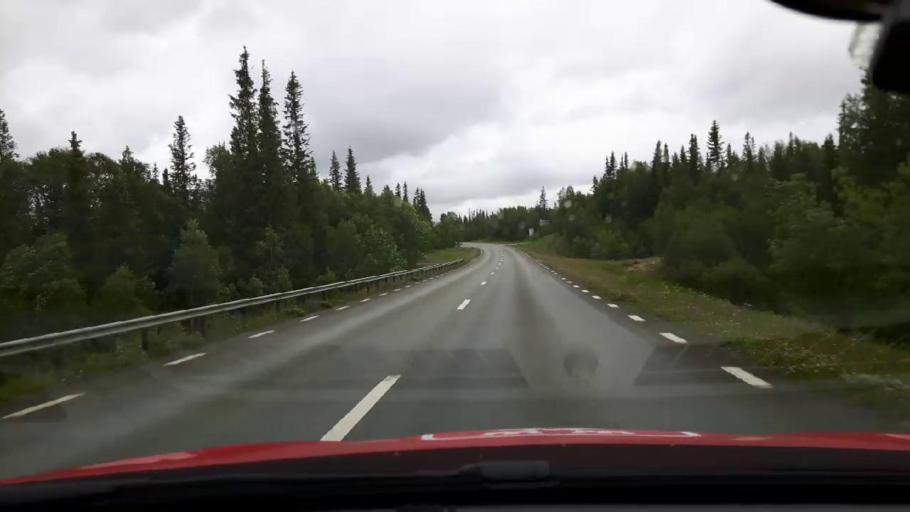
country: NO
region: Nord-Trondelag
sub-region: Meraker
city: Meraker
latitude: 63.2702
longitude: 12.1533
